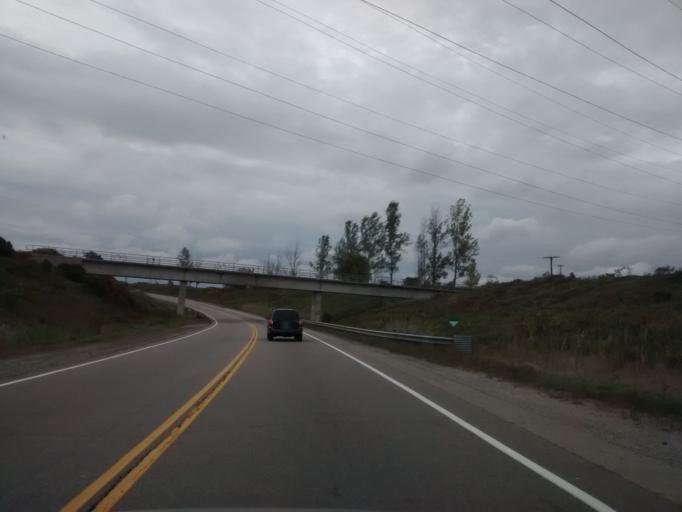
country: CA
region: Ontario
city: Ancaster
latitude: 43.0579
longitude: -79.9807
